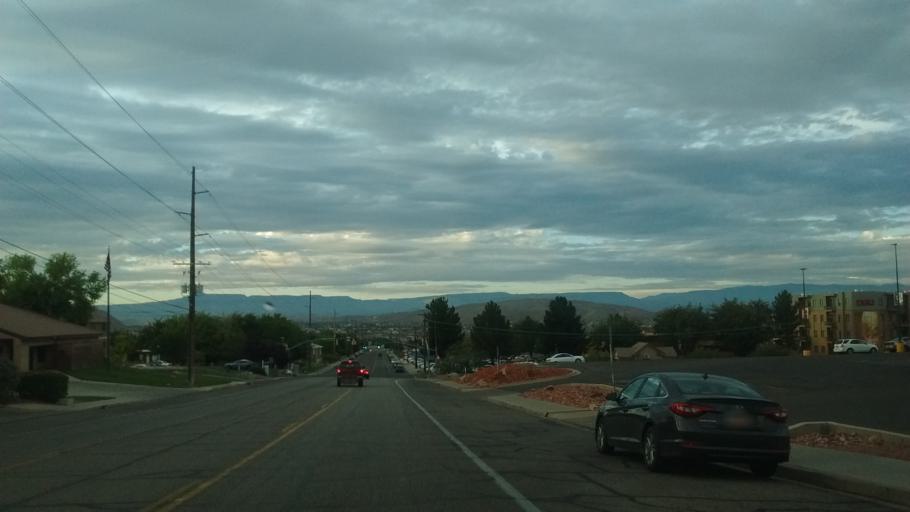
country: US
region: Utah
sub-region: Washington County
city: Saint George
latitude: 37.1078
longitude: -113.5622
